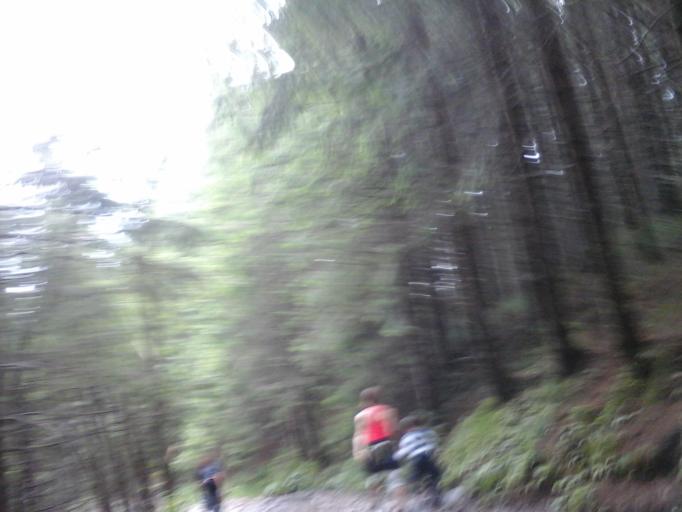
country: PL
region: Lesser Poland Voivodeship
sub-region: Powiat tatrzanski
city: Zakopane
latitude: 49.2676
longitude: 19.9880
